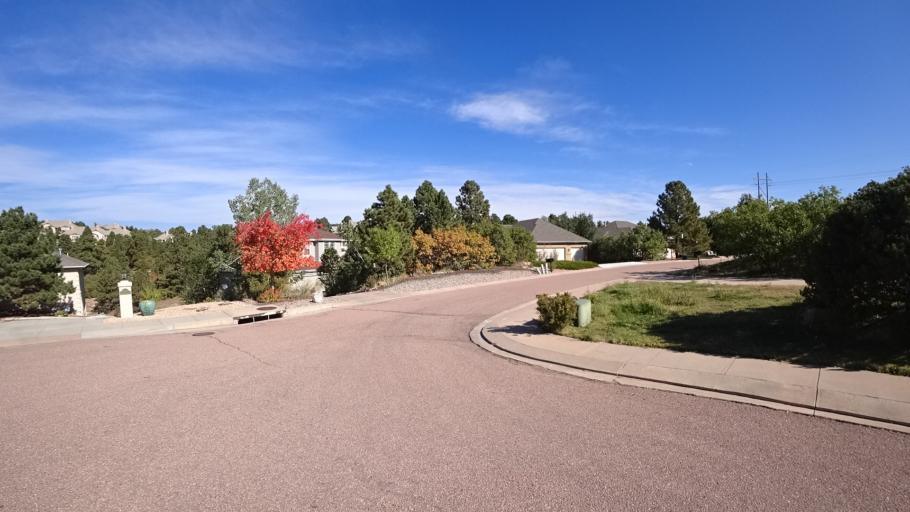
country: US
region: Colorado
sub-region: El Paso County
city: Colorado Springs
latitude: 38.9088
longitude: -104.7905
